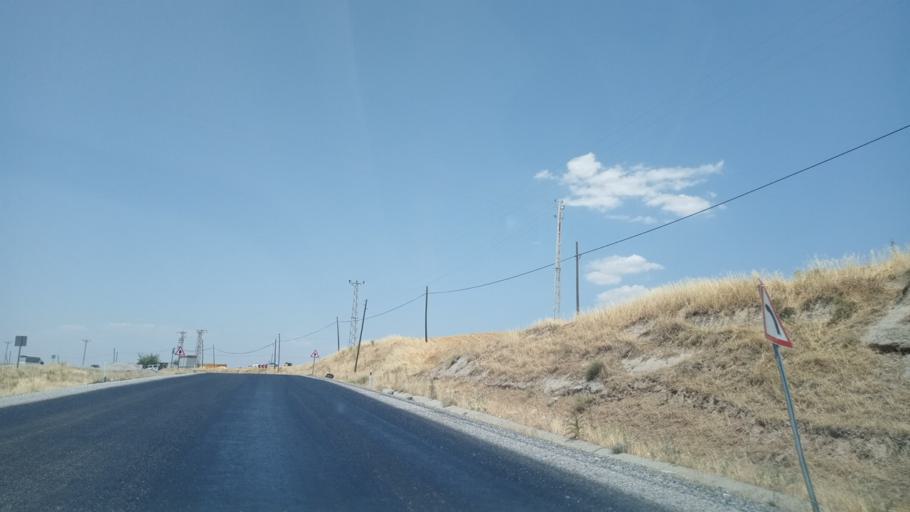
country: TR
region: Batman
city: Bekirhan
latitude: 38.1567
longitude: 41.3750
